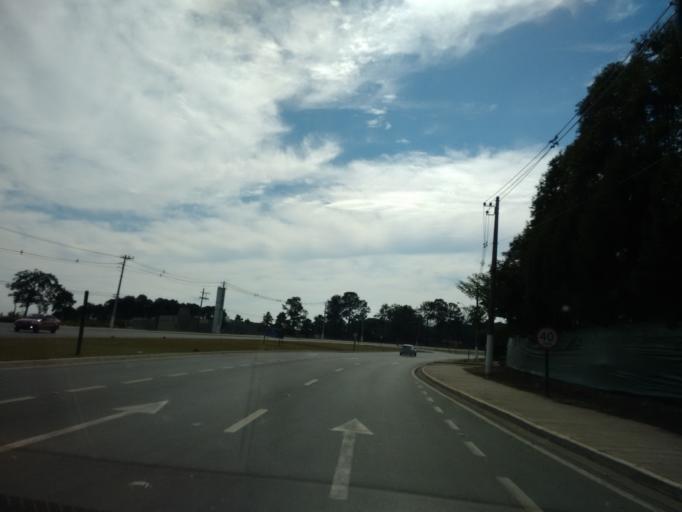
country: BR
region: Sao Paulo
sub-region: Itu
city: Itu
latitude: -23.2935
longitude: -47.3011
